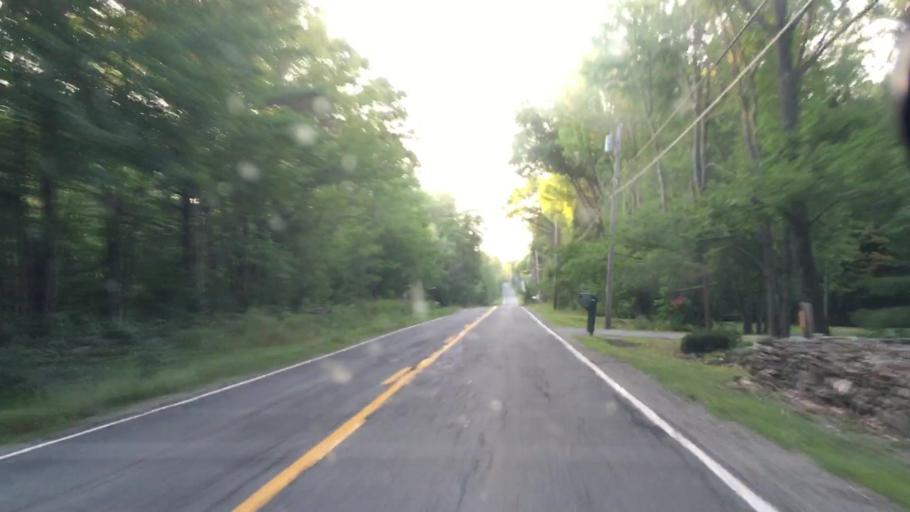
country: US
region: Maine
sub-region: Penobscot County
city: Hermon
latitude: 44.7009
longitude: -68.9458
